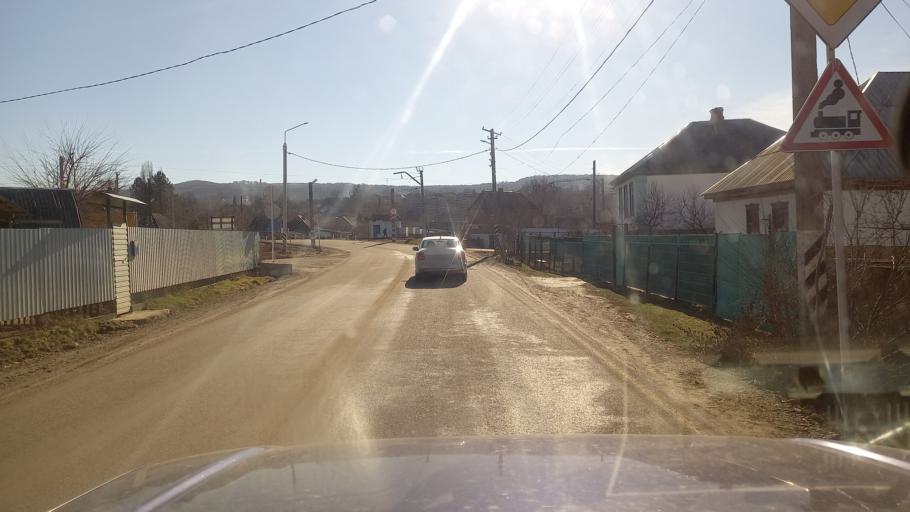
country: RU
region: Adygeya
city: Kamennomostskiy
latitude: 44.2976
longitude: 40.1880
